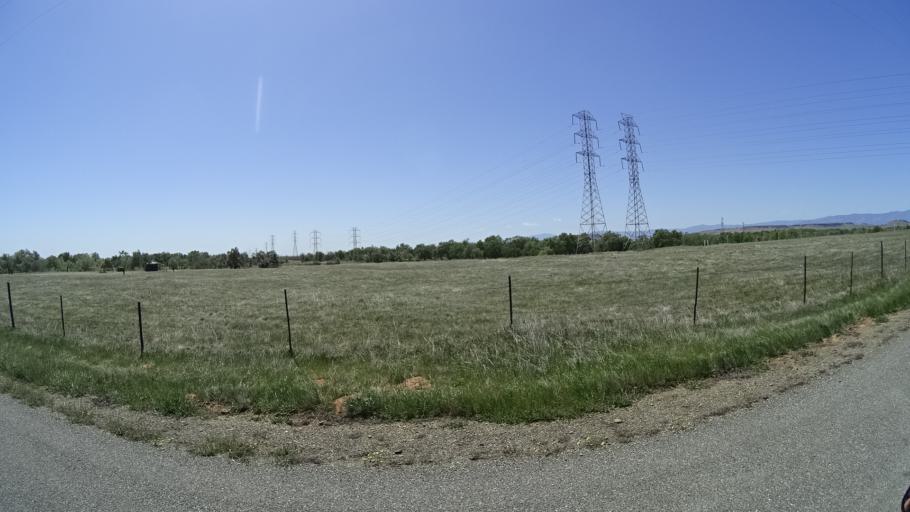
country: US
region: California
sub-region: Glenn County
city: Orland
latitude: 39.7998
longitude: -122.2643
